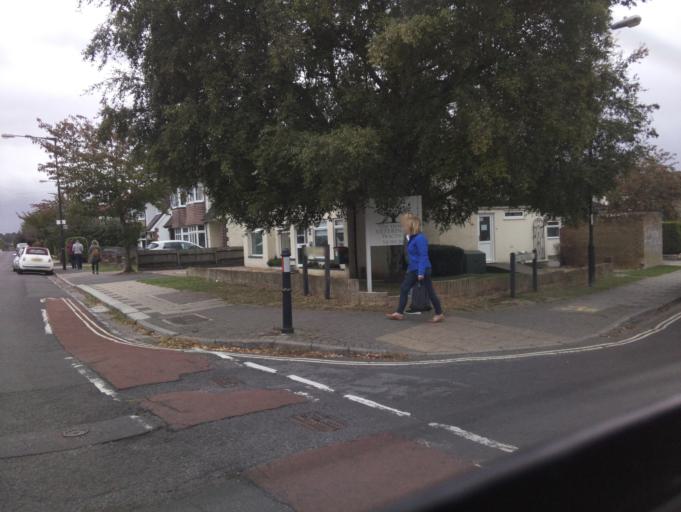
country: GB
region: England
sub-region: Bristol
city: Bristol
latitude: 51.4868
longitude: -2.6242
